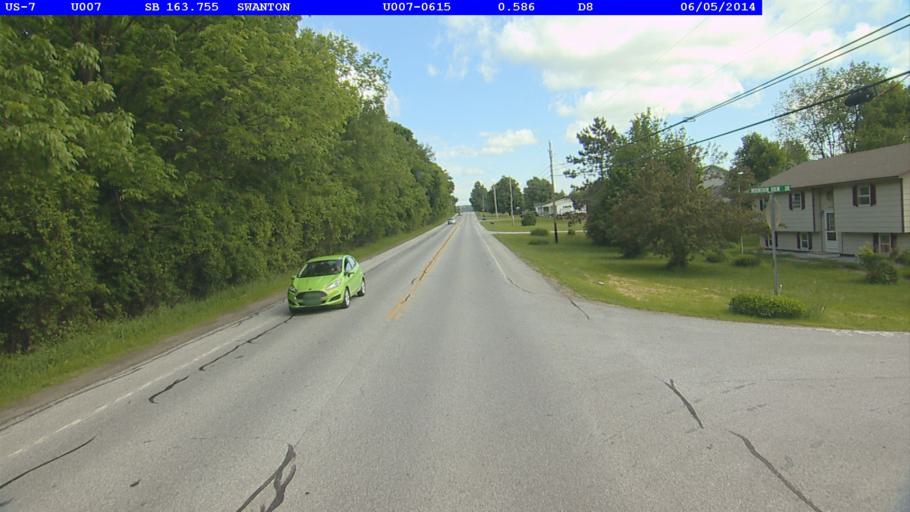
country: US
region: Vermont
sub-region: Franklin County
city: Saint Albans
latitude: 44.8567
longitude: -73.0938
